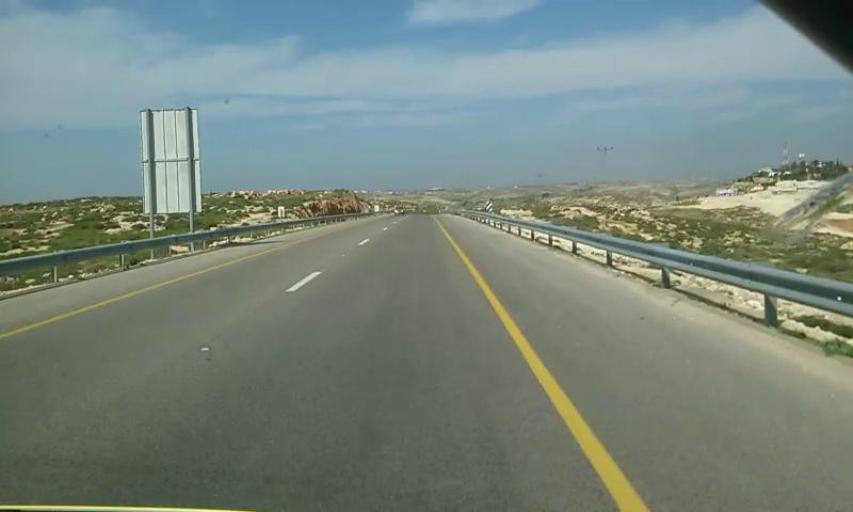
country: PS
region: West Bank
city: Az Zahiriyah
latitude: 31.3821
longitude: 35.0050
